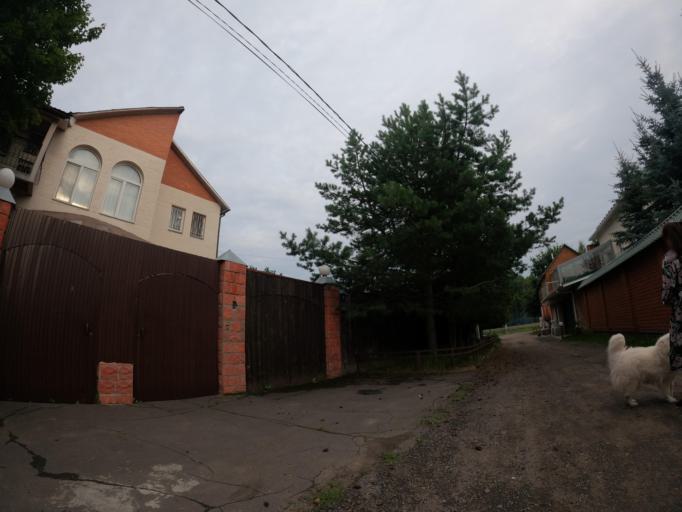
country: RU
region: Moskovskaya
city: Bykovo
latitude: 55.6529
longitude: 38.1093
